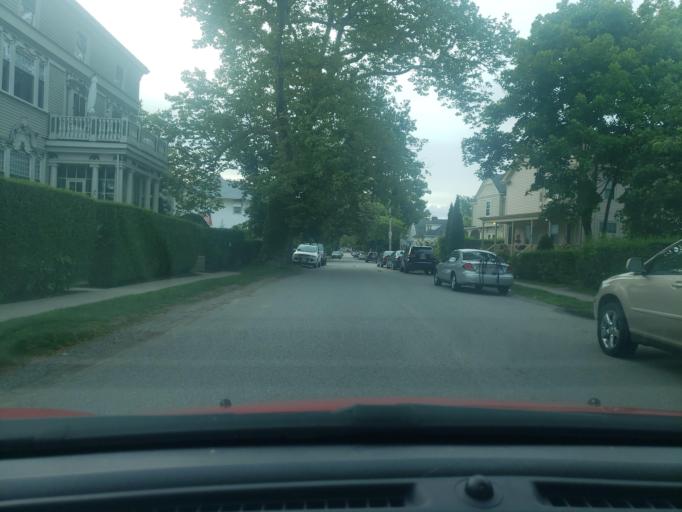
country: US
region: Rhode Island
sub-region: Newport County
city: Newport
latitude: 41.4798
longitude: -71.3063
